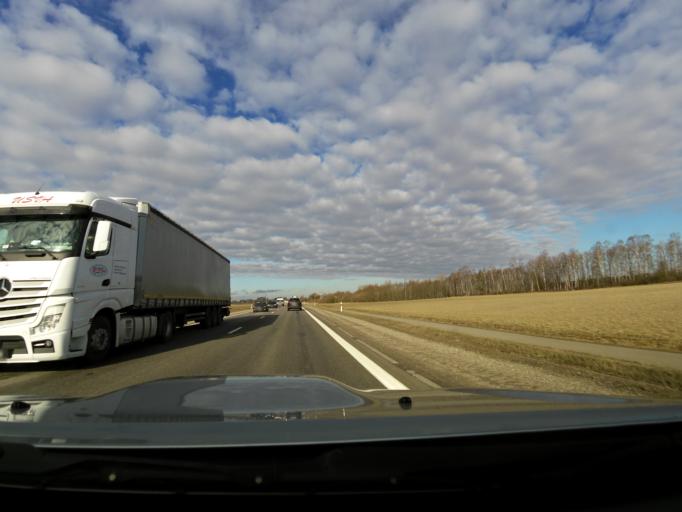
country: LT
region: Panevezys
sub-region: Panevezys City
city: Panevezys
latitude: 55.7405
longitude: 24.1887
